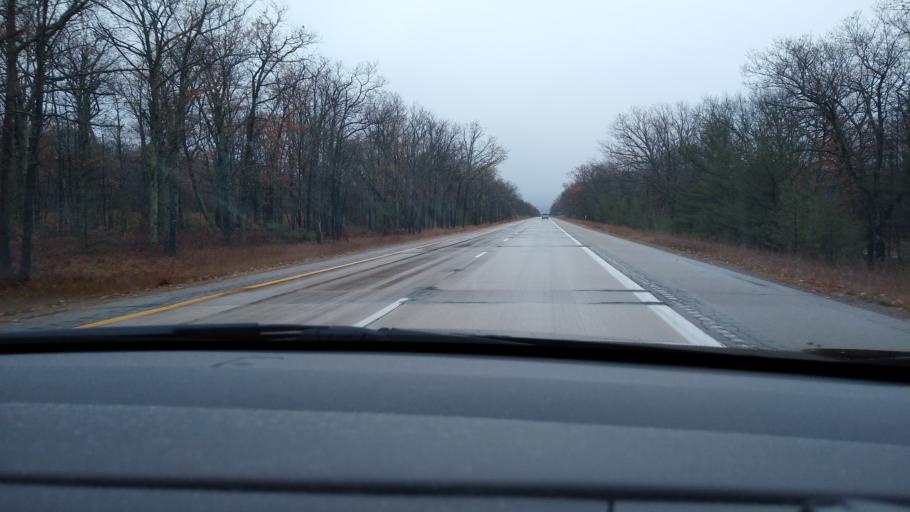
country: US
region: Michigan
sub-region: Cheboygan County
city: Indian River
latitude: 45.4825
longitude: -84.6159
